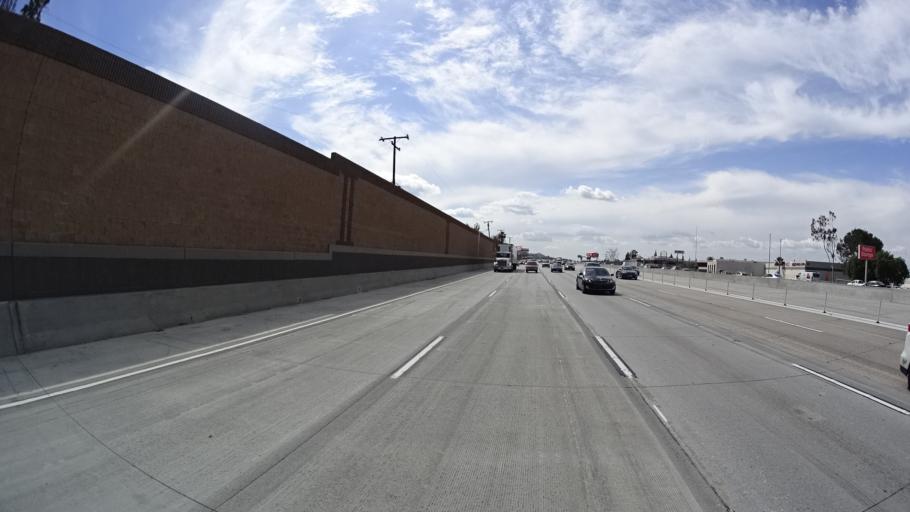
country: US
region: California
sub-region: Riverside County
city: Corona
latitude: 33.8814
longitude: -117.5947
